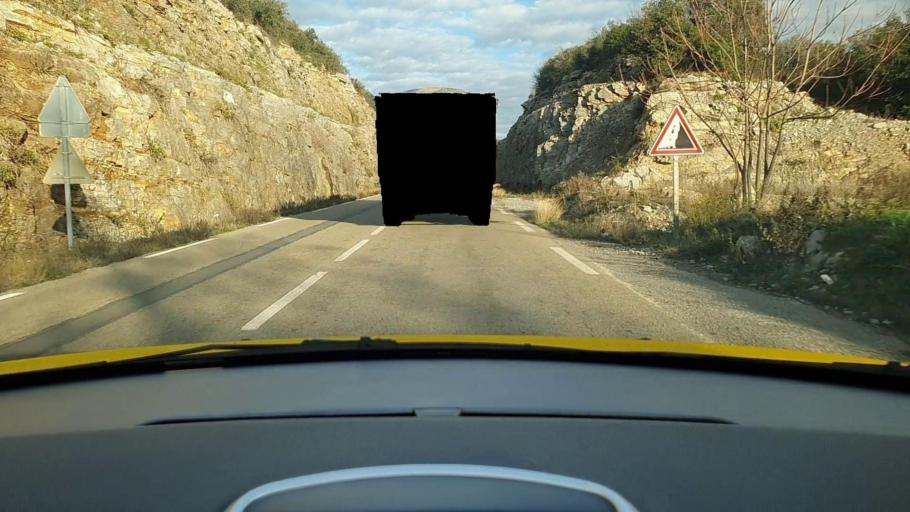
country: FR
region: Languedoc-Roussillon
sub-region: Departement du Gard
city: Saint-Martin-de-Valgalgues
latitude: 44.1738
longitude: 4.0820
